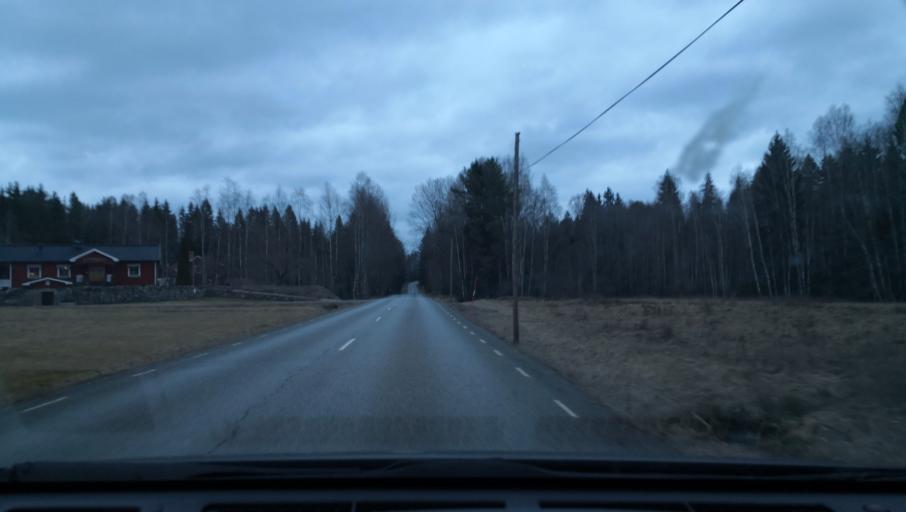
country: SE
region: Vaestmanland
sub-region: Kopings Kommun
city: Kolsva
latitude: 59.5875
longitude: 15.8078
